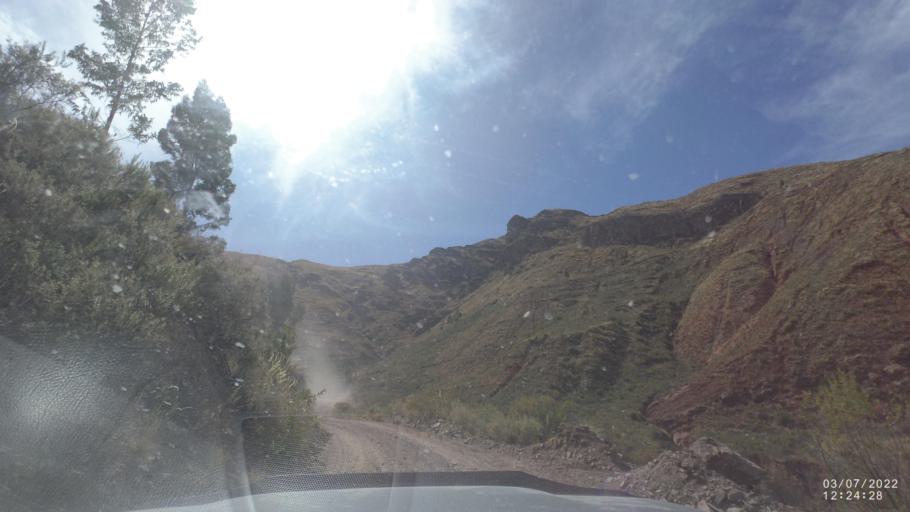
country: BO
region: Cochabamba
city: Irpa Irpa
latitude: -17.8131
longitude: -66.6172
